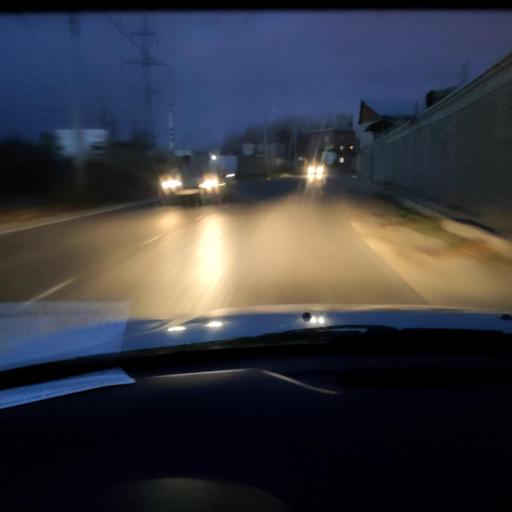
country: RU
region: Samara
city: Zhigulevsk
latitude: 53.5170
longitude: 49.4792
